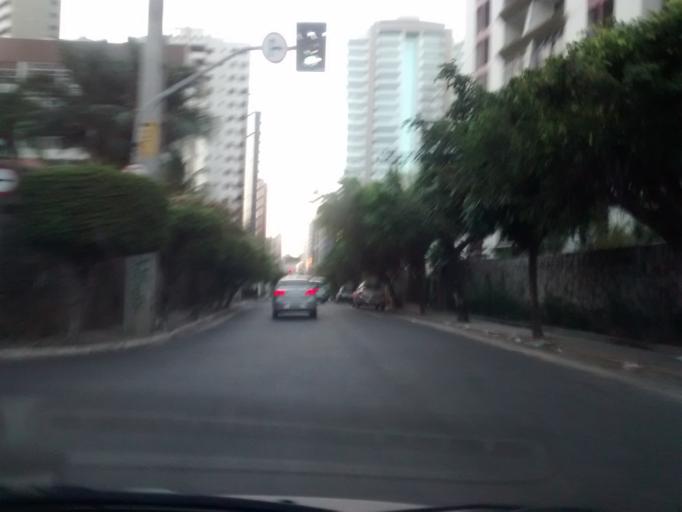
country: BR
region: Ceara
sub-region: Fortaleza
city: Fortaleza
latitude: -3.7458
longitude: -38.4796
